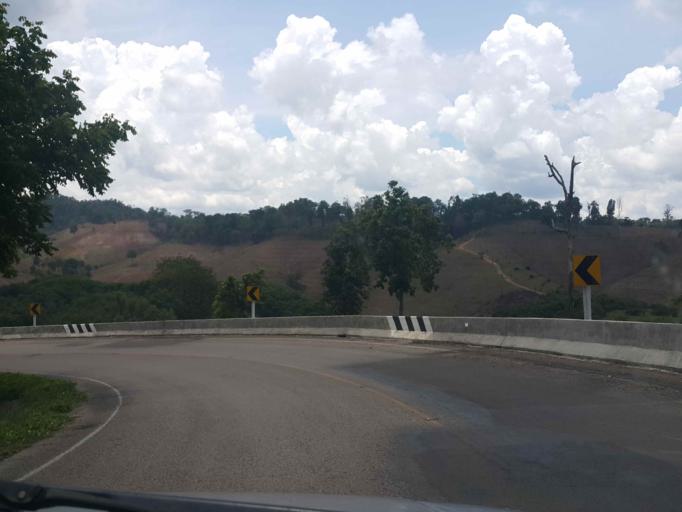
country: TH
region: Phayao
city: Chiang Muan
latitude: 18.9256
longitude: 100.1017
